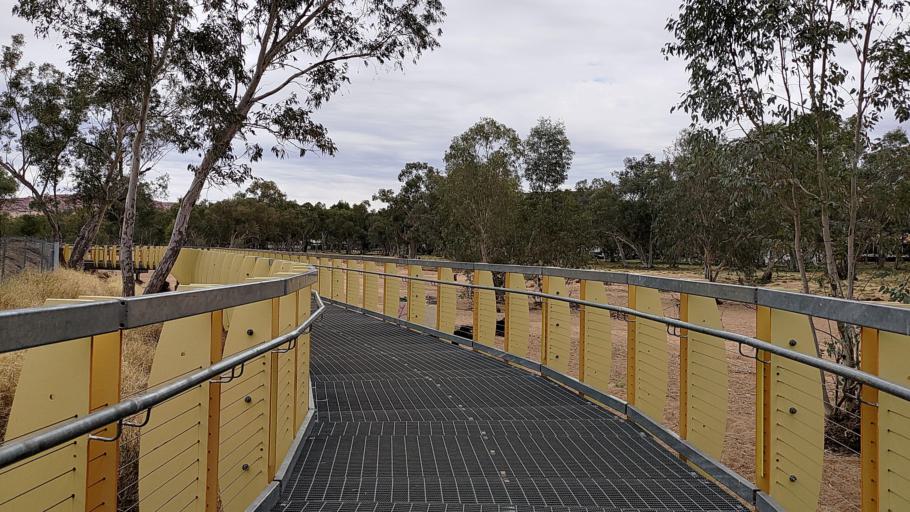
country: AU
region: Northern Territory
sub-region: Alice Springs
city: Alice Springs
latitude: -23.7038
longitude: 133.8841
